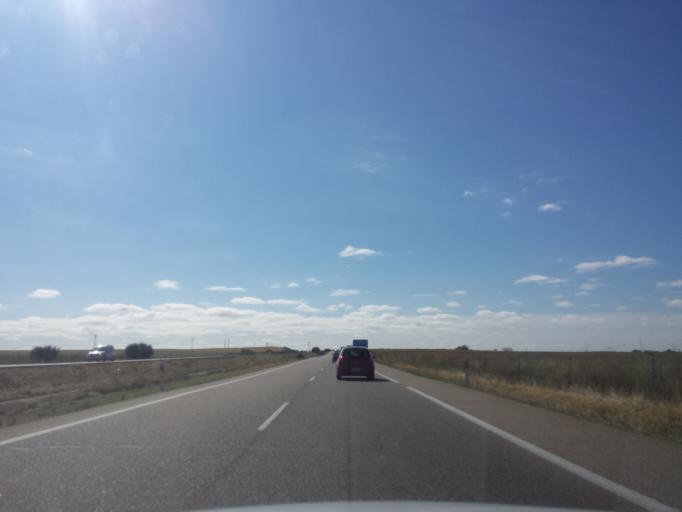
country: ES
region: Castille and Leon
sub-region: Provincia de Zamora
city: San Esteban del Molar
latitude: 41.9531
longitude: -5.5709
